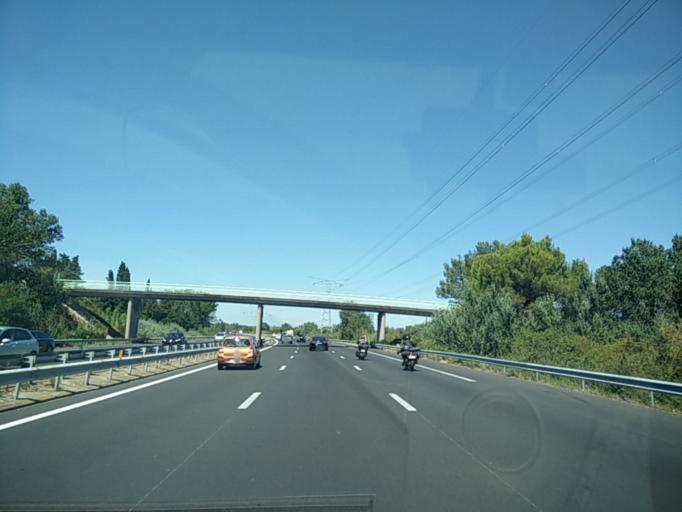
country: FR
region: Provence-Alpes-Cote d'Azur
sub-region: Departement des Bouches-du-Rhone
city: Cabannes
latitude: 43.8500
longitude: 4.9881
